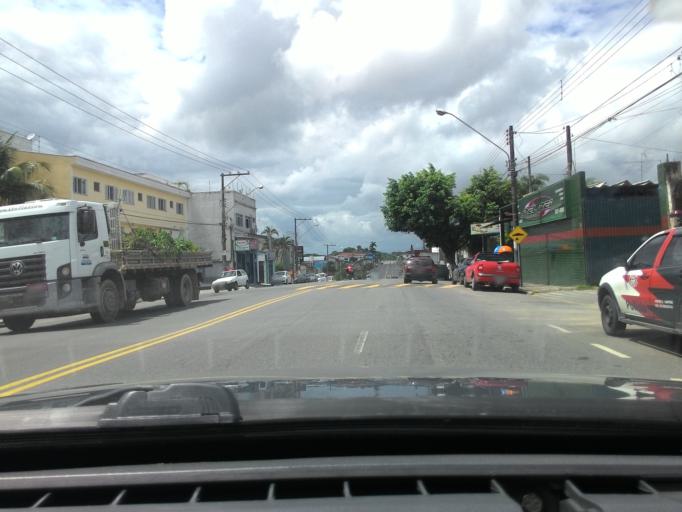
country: BR
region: Sao Paulo
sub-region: Registro
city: Registro
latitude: -24.5004
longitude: -47.8411
